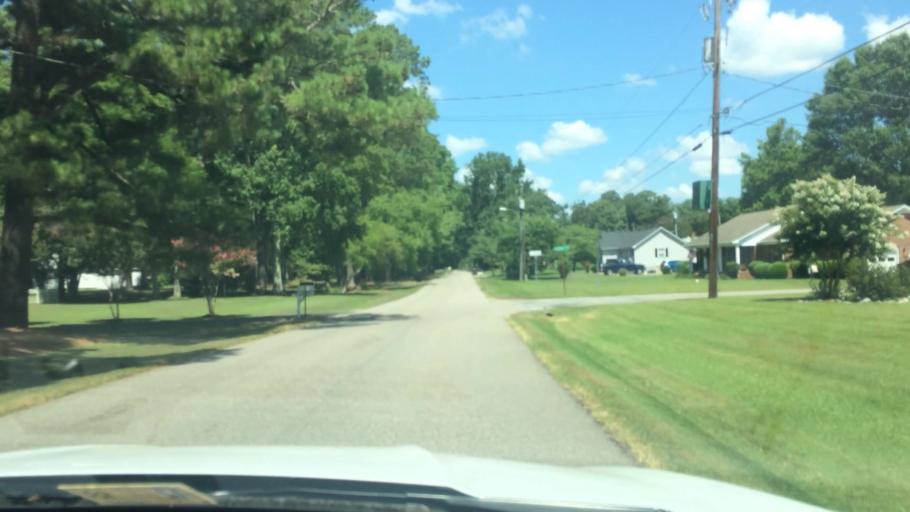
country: US
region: Virginia
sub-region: King William County
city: West Point
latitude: 37.5677
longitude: -76.8041
